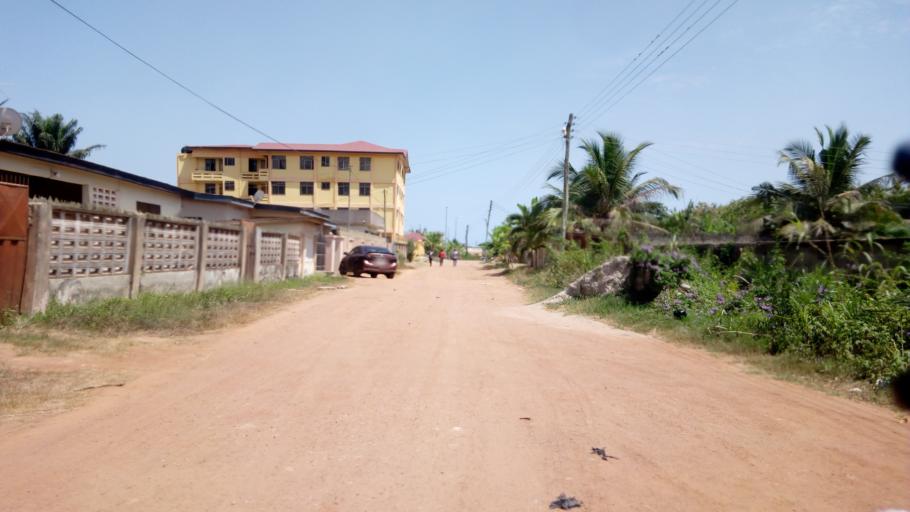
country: GH
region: Central
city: Cape Coast
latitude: 5.1331
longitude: -1.2828
